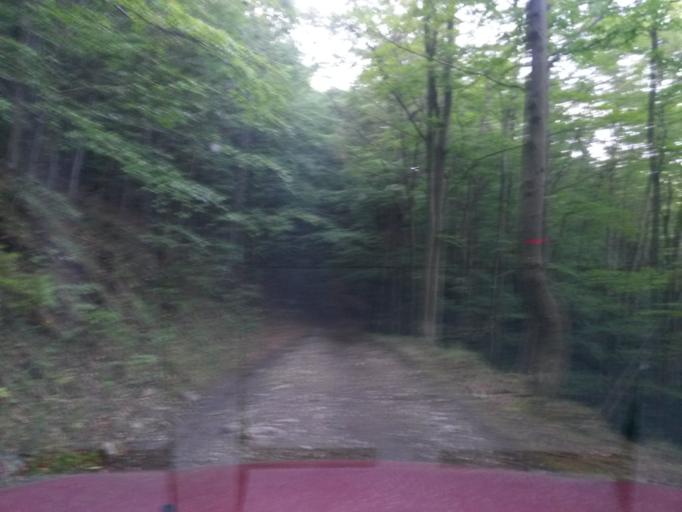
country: SK
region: Kosicky
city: Moldava nad Bodvou
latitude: 48.7328
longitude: 21.0638
